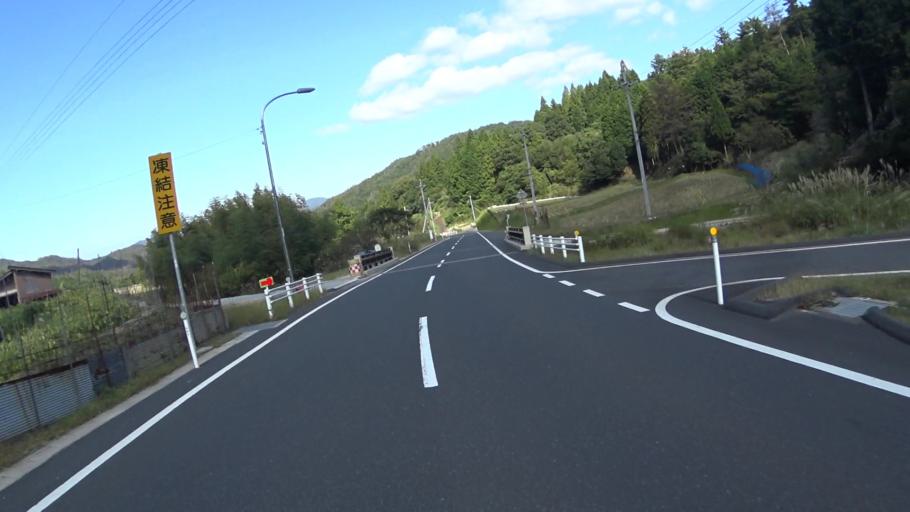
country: JP
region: Hyogo
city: Toyooka
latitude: 35.5404
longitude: 134.9785
